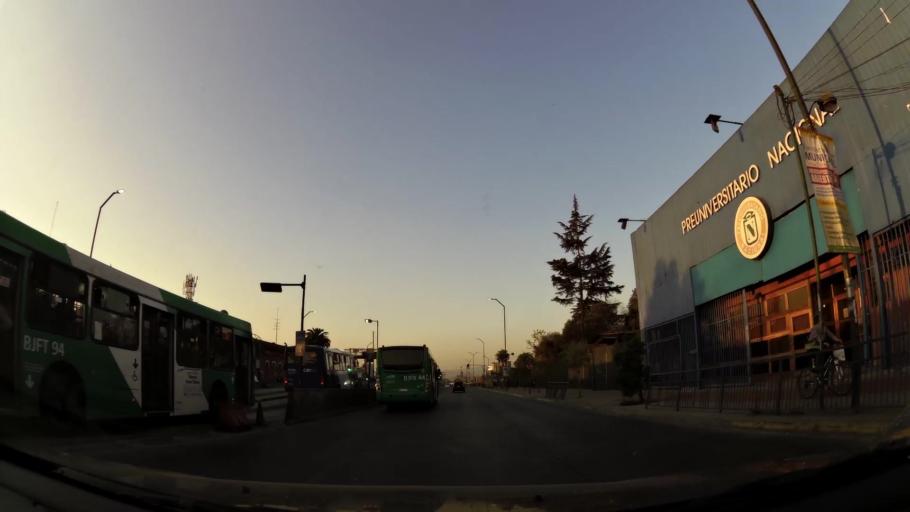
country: CL
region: Santiago Metropolitan
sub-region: Provincia de Santiago
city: La Pintana
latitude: -33.5413
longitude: -70.6652
